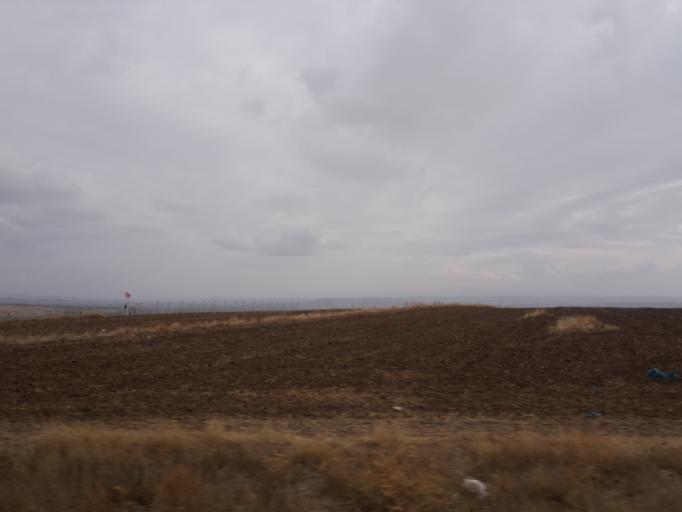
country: TR
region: Kirikkale
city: Celebi
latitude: 39.5106
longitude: 33.5476
